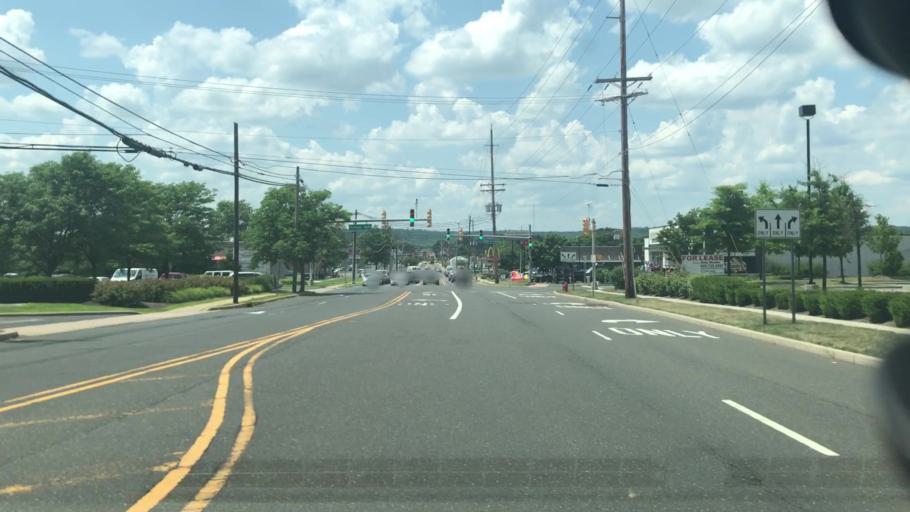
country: US
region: New Jersey
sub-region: Hunterdon County
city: Flemington
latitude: 40.4988
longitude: -74.8525
